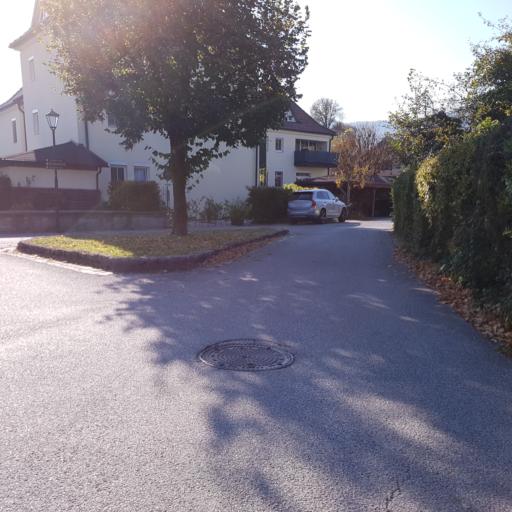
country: AT
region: Salzburg
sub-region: Politischer Bezirk Salzburg-Umgebung
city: Anif
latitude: 47.7279
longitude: 13.0628
